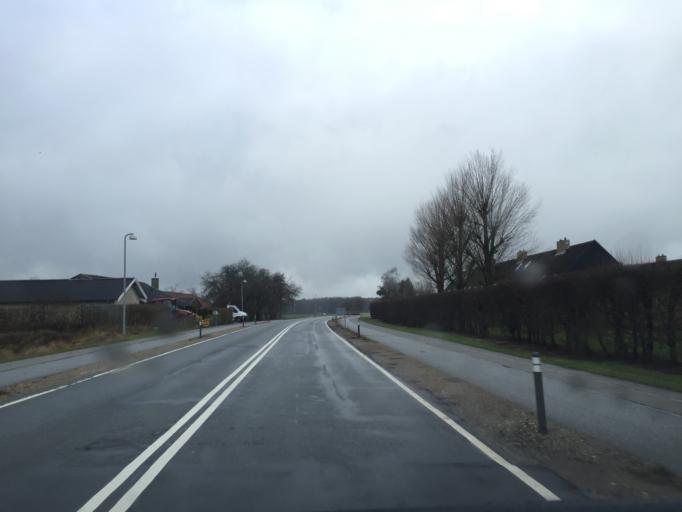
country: DK
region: Capital Region
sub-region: Fureso Kommune
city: Farum
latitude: 55.8133
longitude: 12.3462
